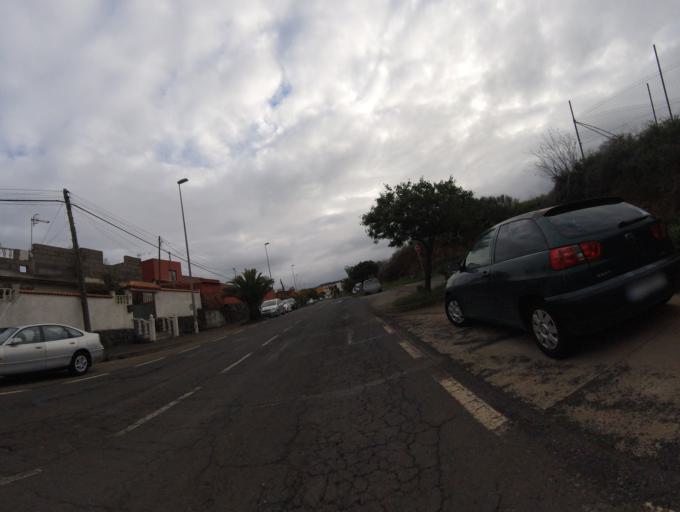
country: ES
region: Canary Islands
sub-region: Provincia de Santa Cruz de Tenerife
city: La Laguna
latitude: 28.4447
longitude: -16.3330
